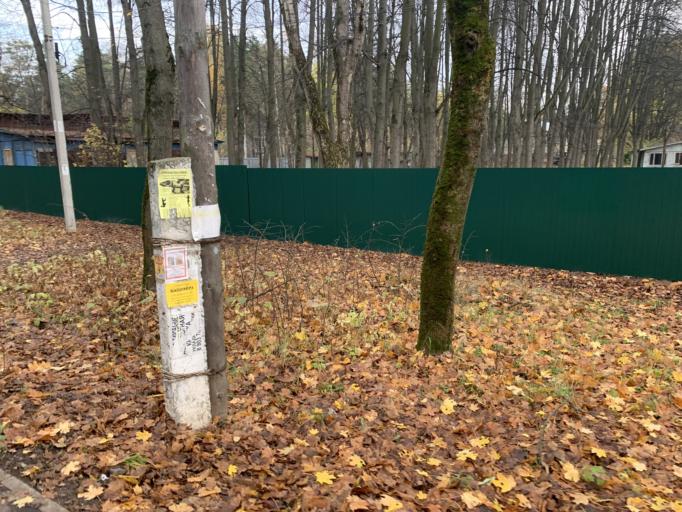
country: RU
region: Moskovskaya
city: Mamontovka
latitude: 55.9831
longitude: 37.8364
